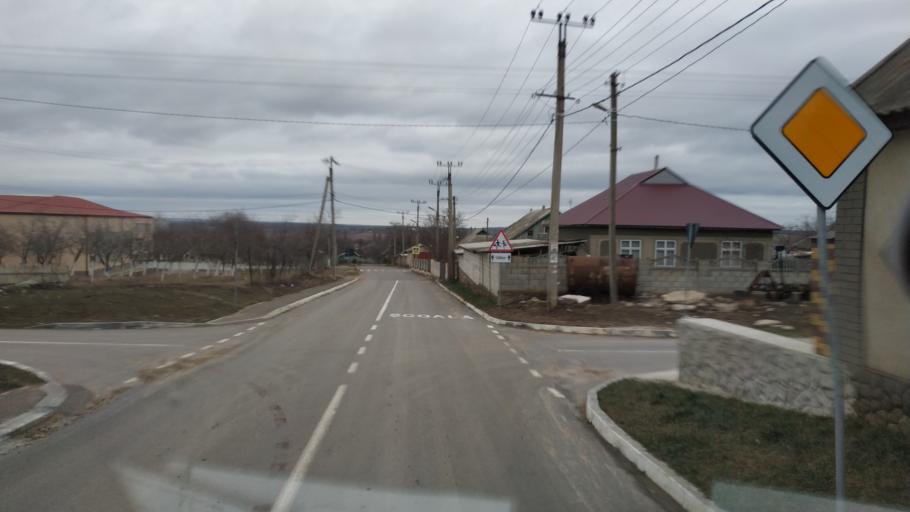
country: MD
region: Bender
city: Bender
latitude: 46.7779
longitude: 29.4787
